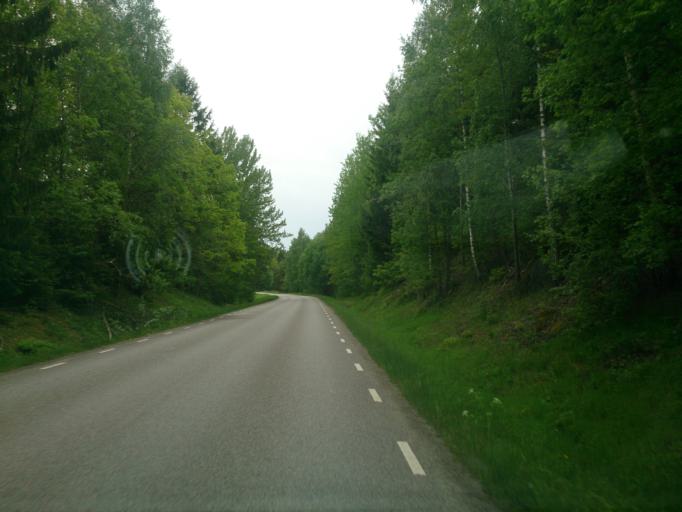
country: SE
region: OEstergoetland
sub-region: Atvidabergs Kommun
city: Atvidaberg
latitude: 58.2488
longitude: 16.0161
